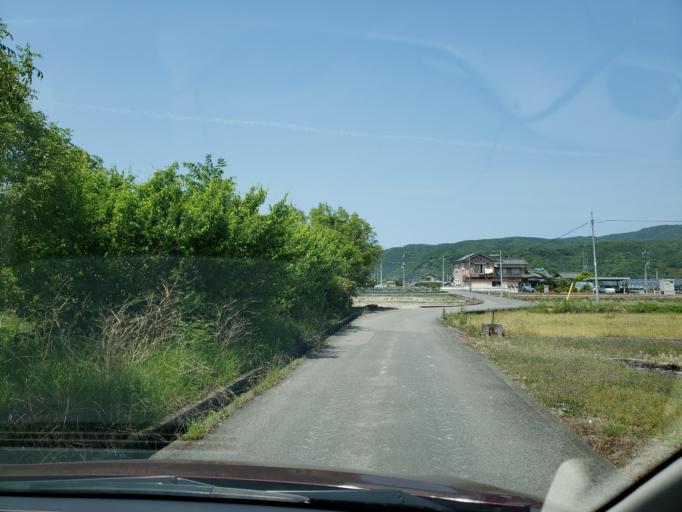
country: JP
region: Tokushima
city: Kamojimacho-jogejima
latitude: 34.0972
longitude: 134.2687
